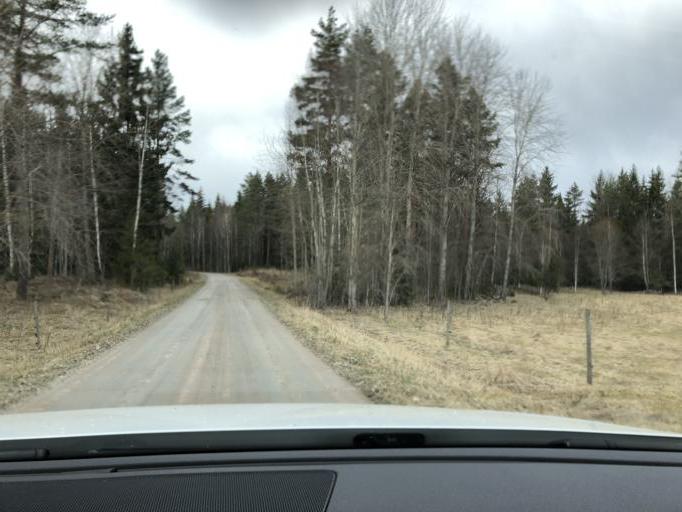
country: SE
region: Gaevleborg
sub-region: Gavle Kommun
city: Hedesunda
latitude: 60.3177
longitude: 17.1052
